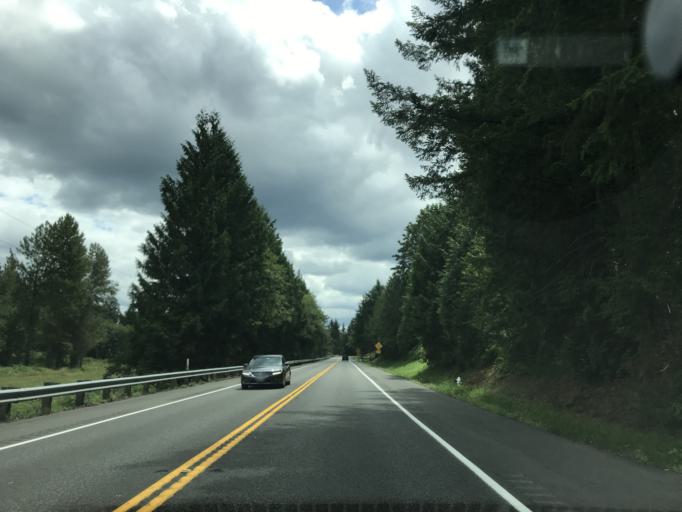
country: US
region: Washington
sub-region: King County
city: Maple Valley
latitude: 47.4074
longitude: -122.0515
